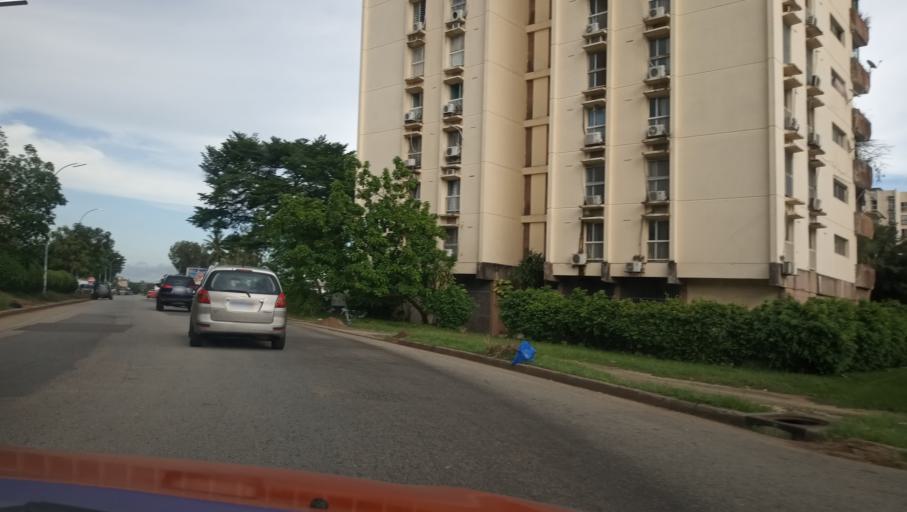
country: CI
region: Lagunes
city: Abidjan
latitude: 5.3410
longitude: -3.9788
